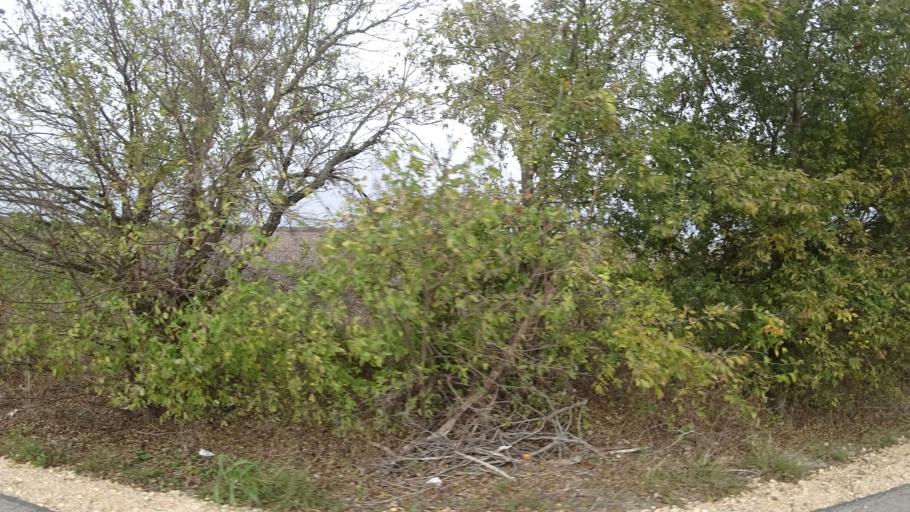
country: US
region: Texas
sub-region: Travis County
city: Manor
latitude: 30.3863
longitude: -97.5541
